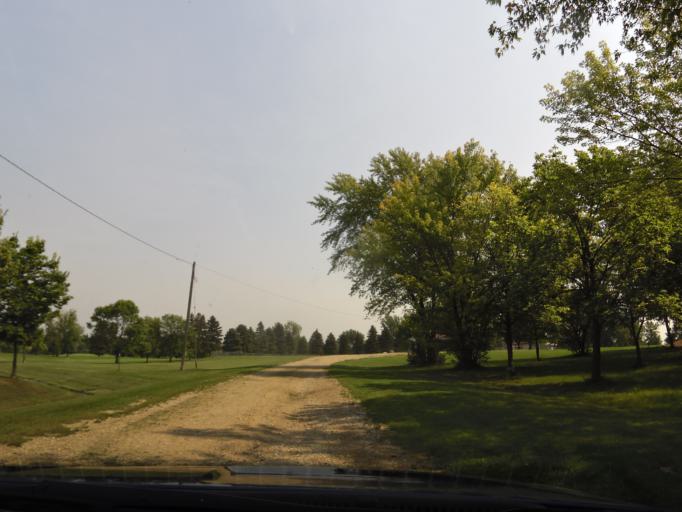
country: US
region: South Dakota
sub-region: Roberts County
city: Sisseton
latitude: 46.0733
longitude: -97.1414
